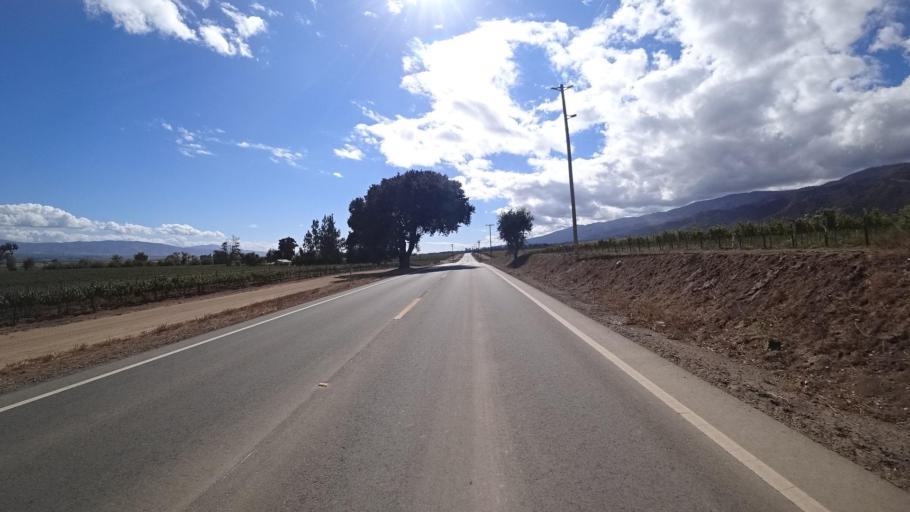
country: US
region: California
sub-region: Monterey County
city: Gonzales
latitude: 36.4934
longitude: -121.4955
